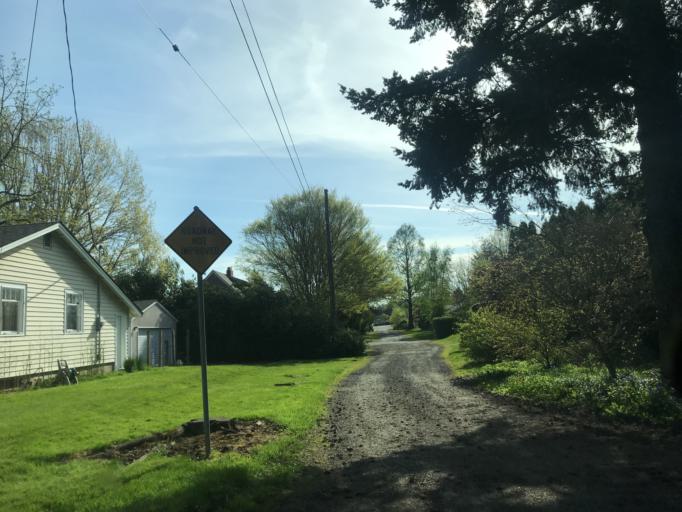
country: US
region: Oregon
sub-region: Multnomah County
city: Lents
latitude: 45.5023
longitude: -122.5986
